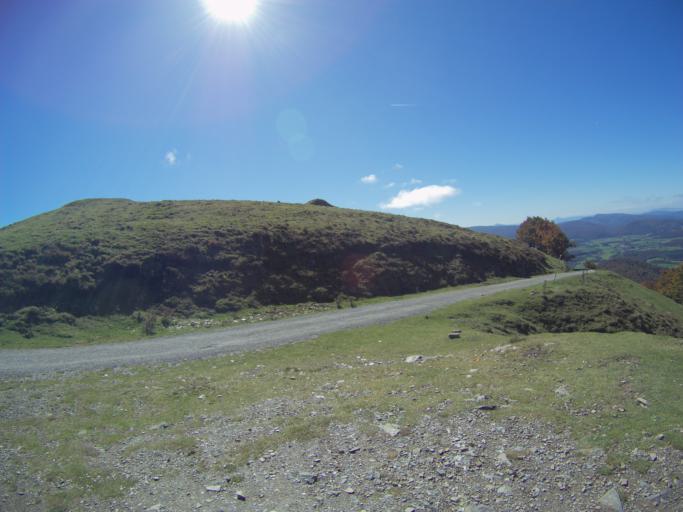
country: ES
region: Navarre
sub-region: Provincia de Navarra
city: Garralda
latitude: 43.0261
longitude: -1.2956
